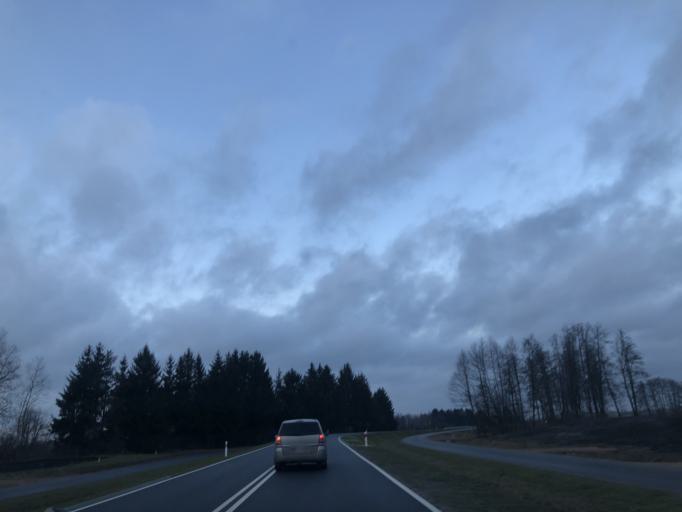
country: PL
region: Podlasie
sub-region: Lomza
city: Lomza
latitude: 53.1270
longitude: 22.0486
